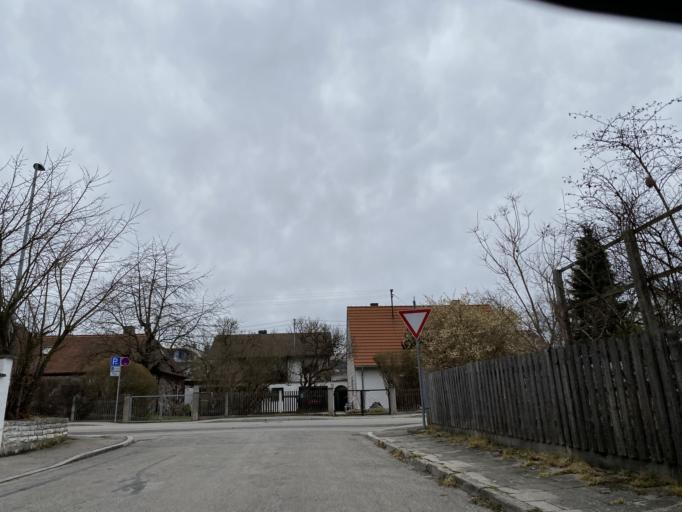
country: DE
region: Bavaria
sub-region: Upper Bavaria
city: Schongeising
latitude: 48.1596
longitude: 11.2275
